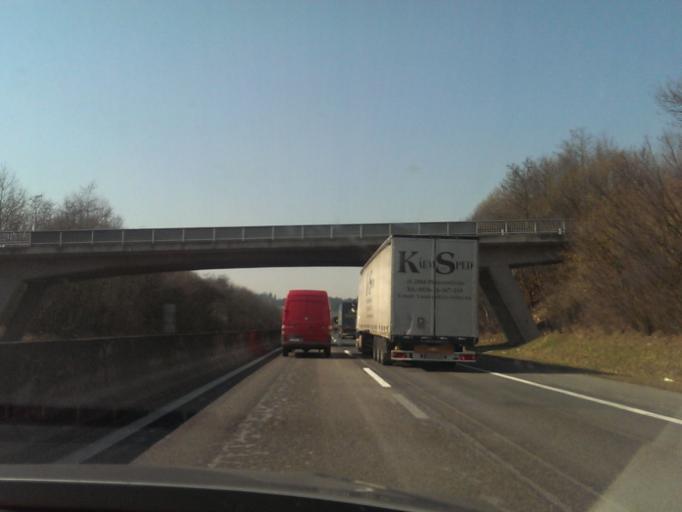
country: AT
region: Upper Austria
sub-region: Politischer Bezirk Ried im Innkreis
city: Ried im Innkreis
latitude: 48.2428
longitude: 13.5403
